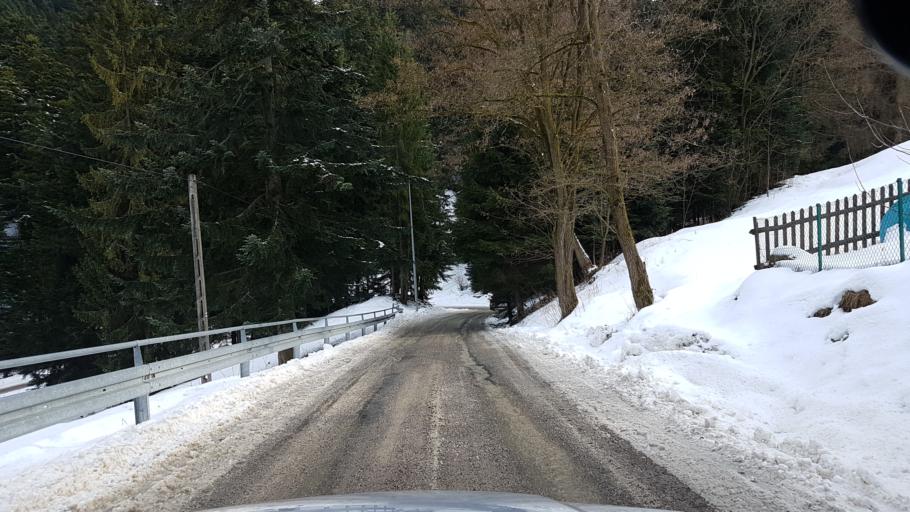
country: PL
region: Lesser Poland Voivodeship
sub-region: Powiat nowosadecki
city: Piwniczna-Zdroj
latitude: 49.4163
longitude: 20.6421
